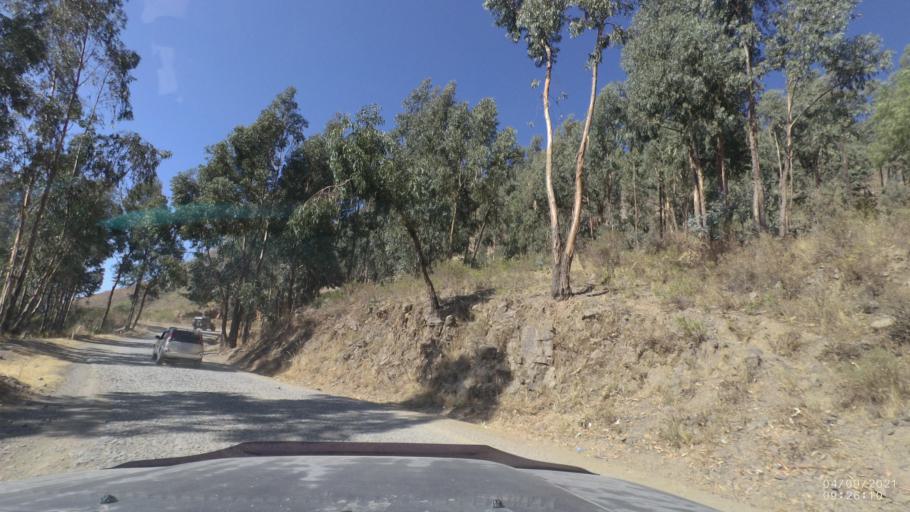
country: BO
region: Cochabamba
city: Sipe Sipe
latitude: -17.3571
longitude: -66.3712
